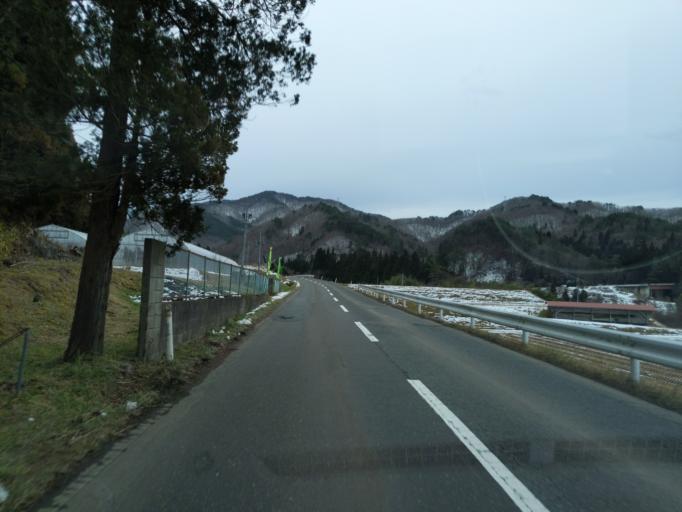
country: JP
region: Iwate
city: Mizusawa
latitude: 39.1080
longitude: 141.2716
